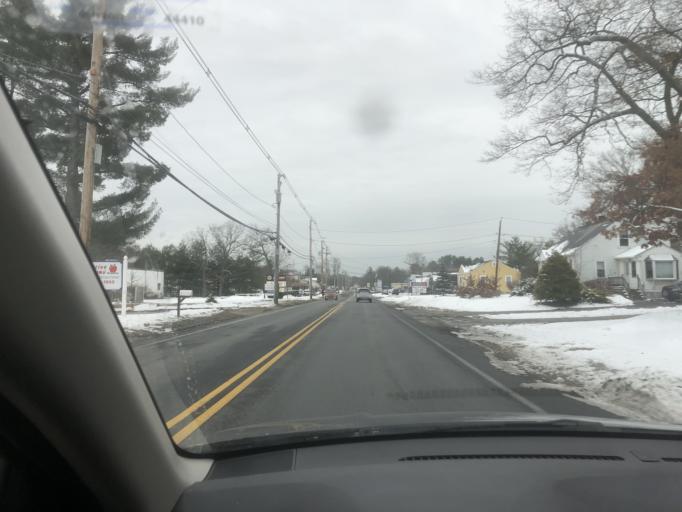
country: US
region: Massachusetts
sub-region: Middlesex County
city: Tewksbury
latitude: 42.6155
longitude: -71.2429
